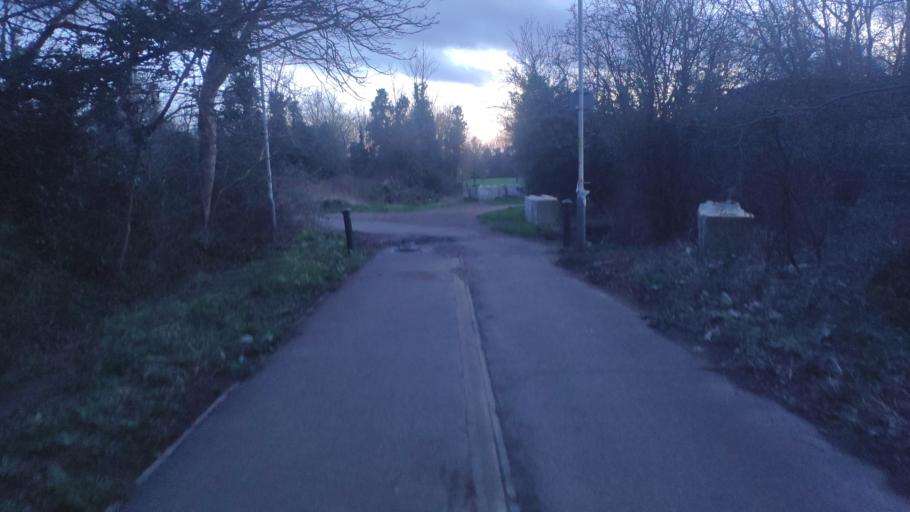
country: GB
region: England
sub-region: Greater London
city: Ruislip
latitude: 51.5733
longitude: -0.4375
